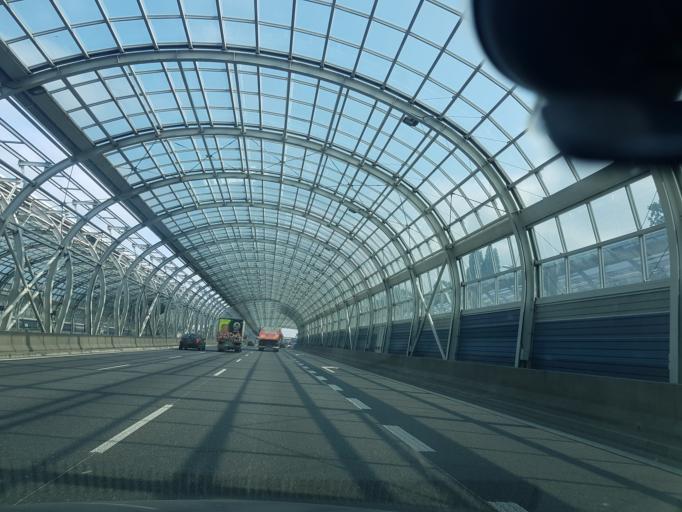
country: PL
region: Masovian Voivodeship
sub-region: Warszawa
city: Targowek
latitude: 52.2959
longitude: 21.0224
